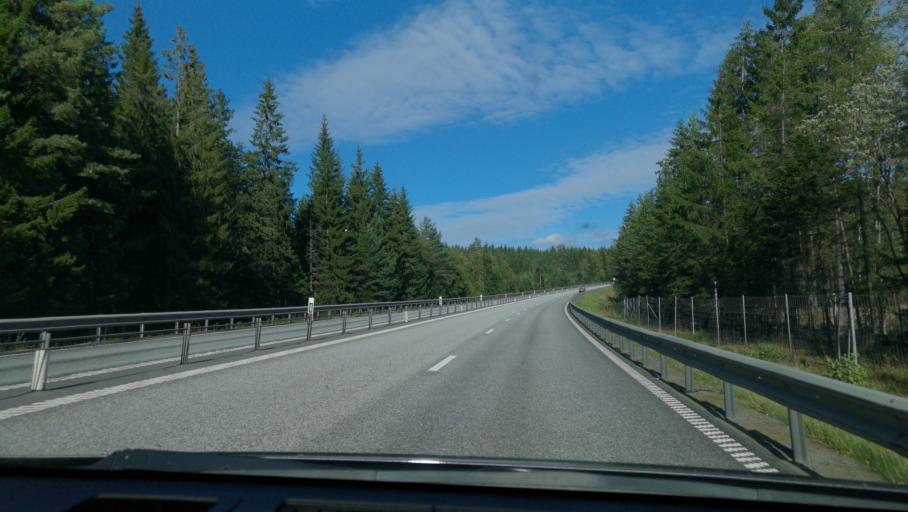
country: SE
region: Vaestra Goetaland
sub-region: Gullspangs Kommun
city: Anderstorp
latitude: 58.9409
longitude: 14.4376
